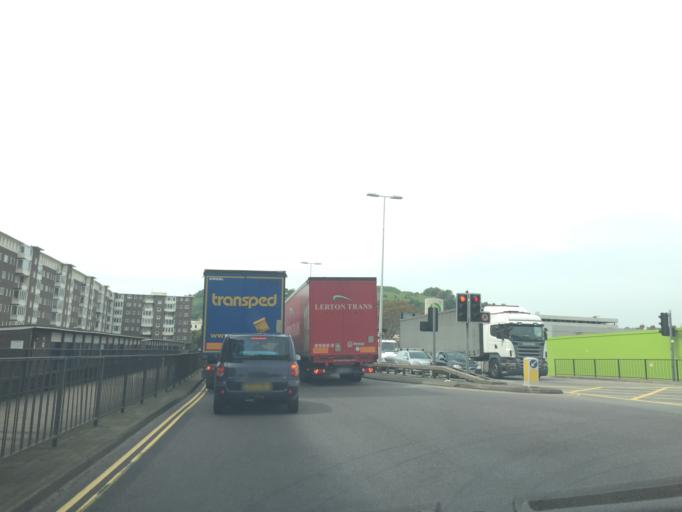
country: GB
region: England
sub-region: Kent
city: Dover
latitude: 51.1251
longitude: 1.3185
